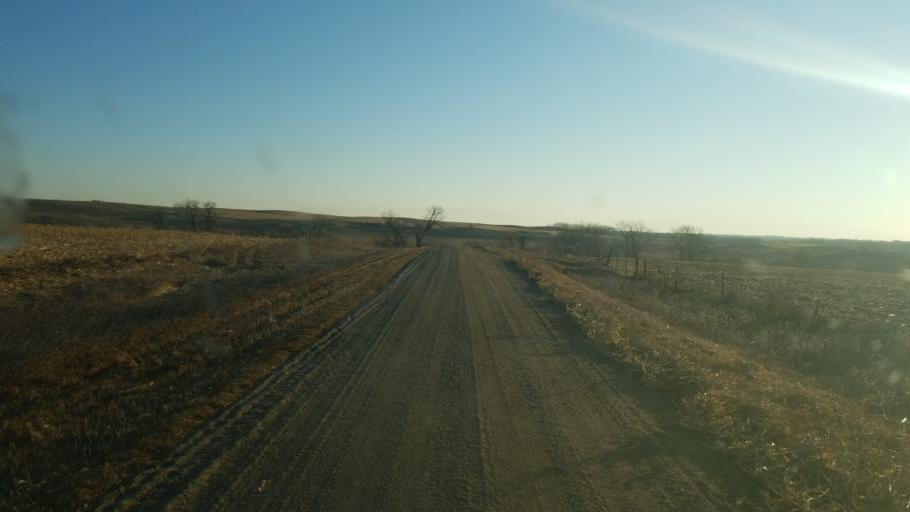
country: US
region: Nebraska
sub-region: Knox County
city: Center
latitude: 42.5609
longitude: -97.7844
